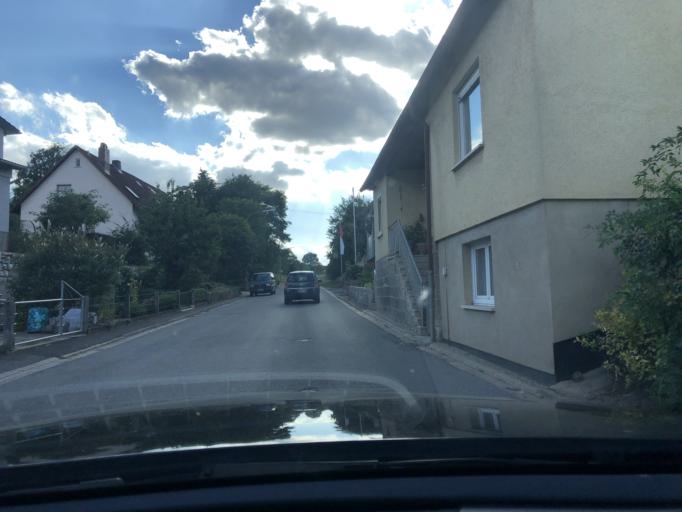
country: DE
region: Bavaria
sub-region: Regierungsbezirk Unterfranken
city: Kirchlauter
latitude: 50.0436
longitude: 10.7118
